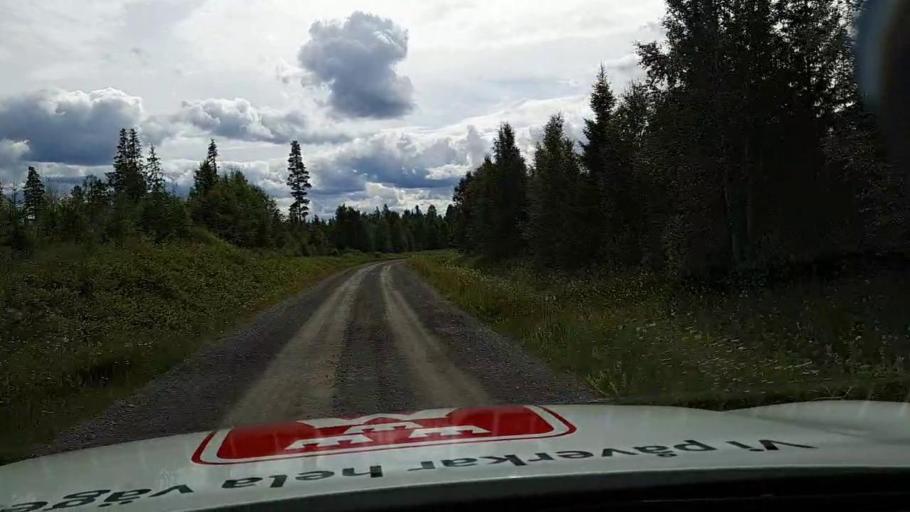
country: SE
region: Jaemtland
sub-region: OEstersunds Kommun
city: Lit
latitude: 63.3033
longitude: 15.2467
